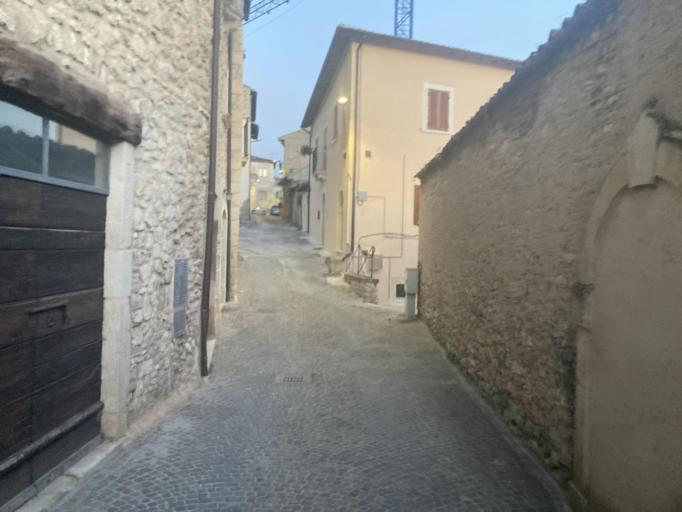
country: IT
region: Abruzzo
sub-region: Provincia dell' Aquila
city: San Demetrio Ne' Vestini
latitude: 42.2915
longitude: 13.5537
